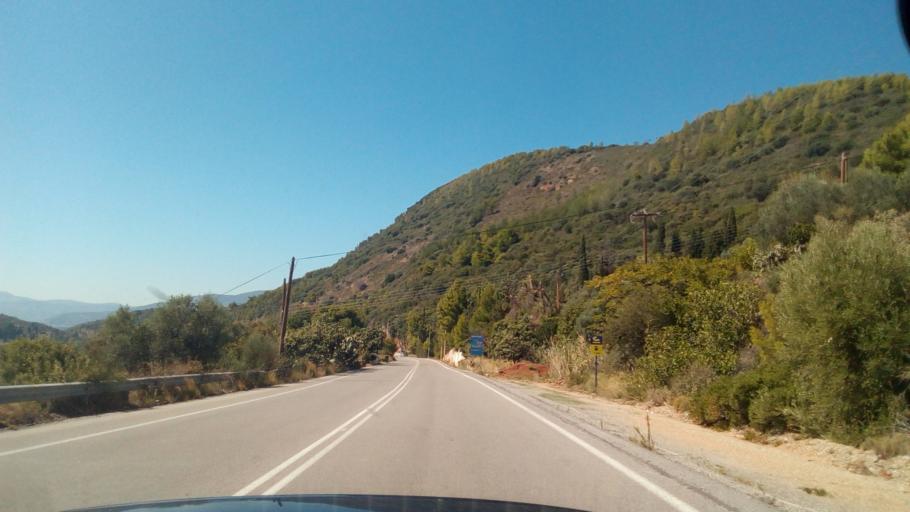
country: GR
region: West Greece
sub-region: Nomos Achaias
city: Kamarai
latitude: 38.4077
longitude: 21.9492
